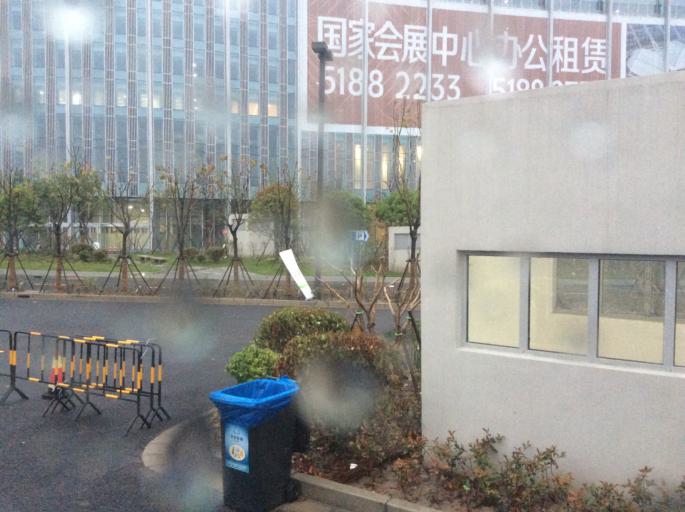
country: CN
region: Shanghai Shi
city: Huacao
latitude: 31.1903
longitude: 121.3025
